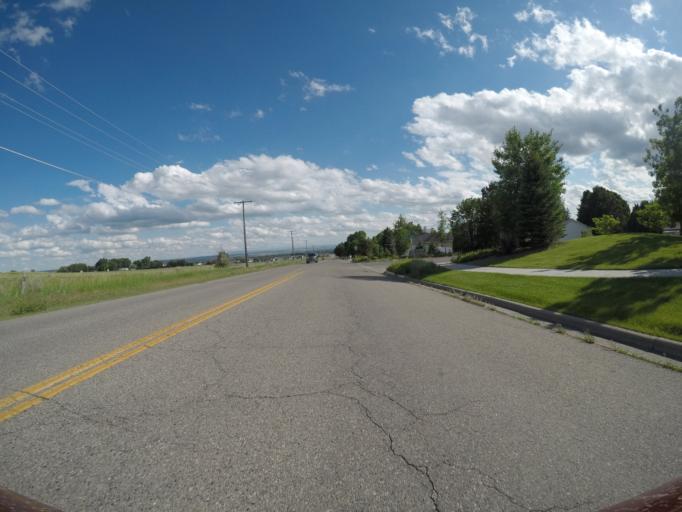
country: US
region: Montana
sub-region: Yellowstone County
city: Billings
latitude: 45.8025
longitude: -108.6527
